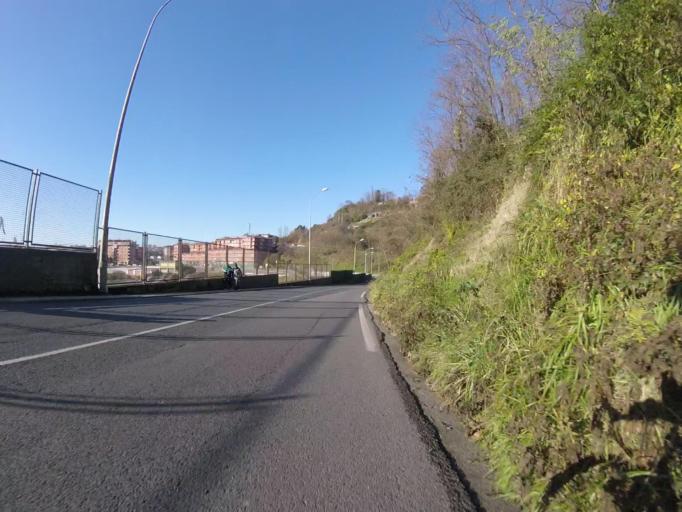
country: ES
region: Basque Country
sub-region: Provincia de Guipuzcoa
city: Lezo
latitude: 43.3241
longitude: -1.9085
